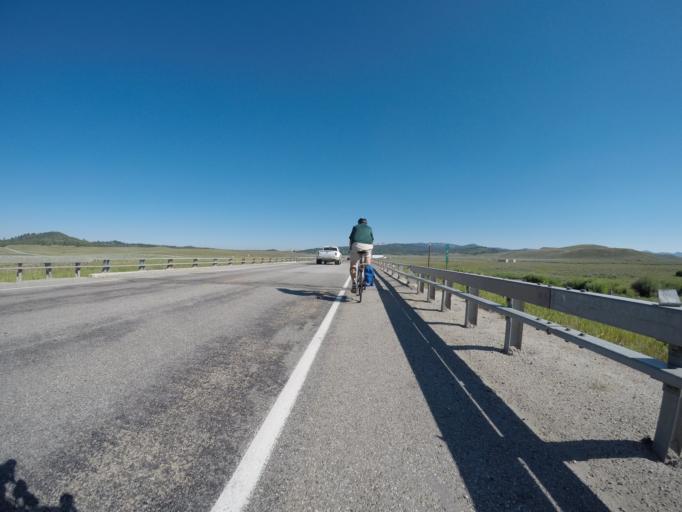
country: US
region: Wyoming
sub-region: Sublette County
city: Pinedale
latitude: 43.1106
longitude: -110.1736
